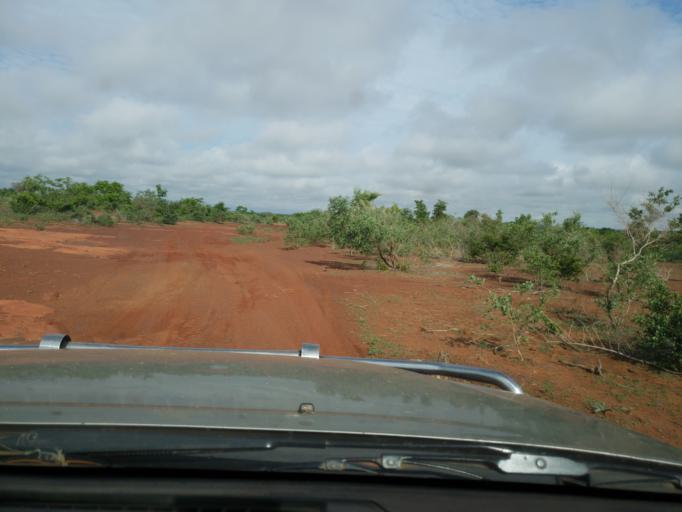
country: ML
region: Sikasso
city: Koutiala
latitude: 12.3925
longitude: -5.9941
